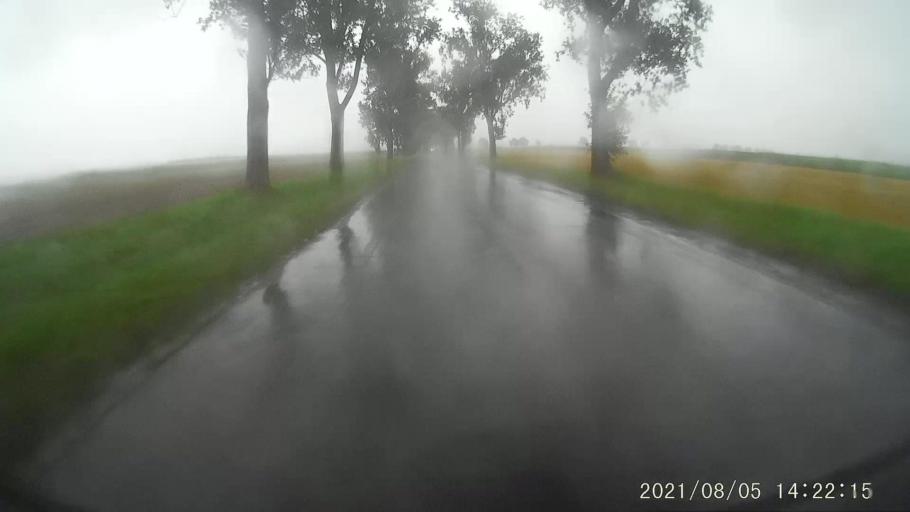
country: PL
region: Opole Voivodeship
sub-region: Powiat nyski
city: Korfantow
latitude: 50.4759
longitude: 17.6594
